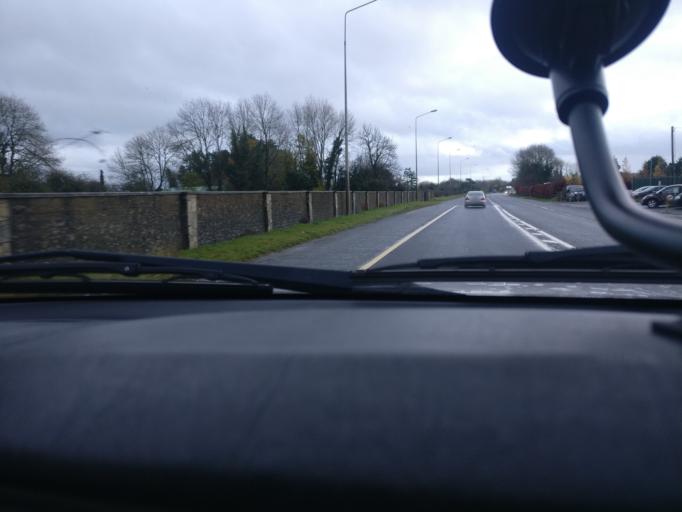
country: IE
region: Leinster
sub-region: Kildare
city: Kilcock
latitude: 53.4111
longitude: -6.7080
